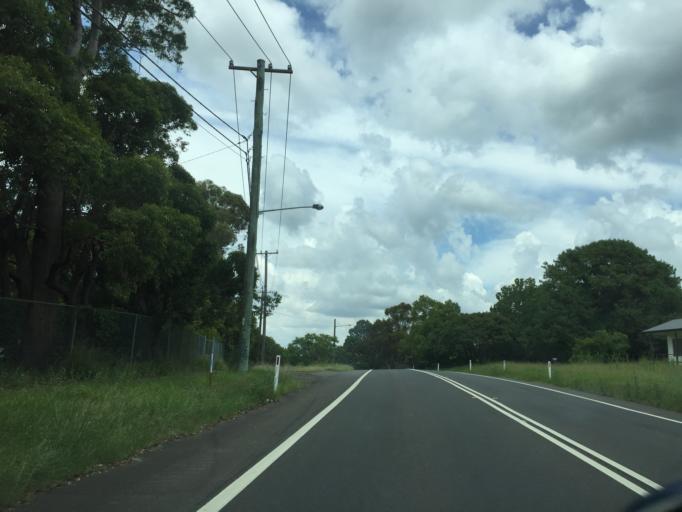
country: AU
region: New South Wales
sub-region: Hornsby Shire
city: Galston
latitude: -33.6538
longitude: 151.0405
